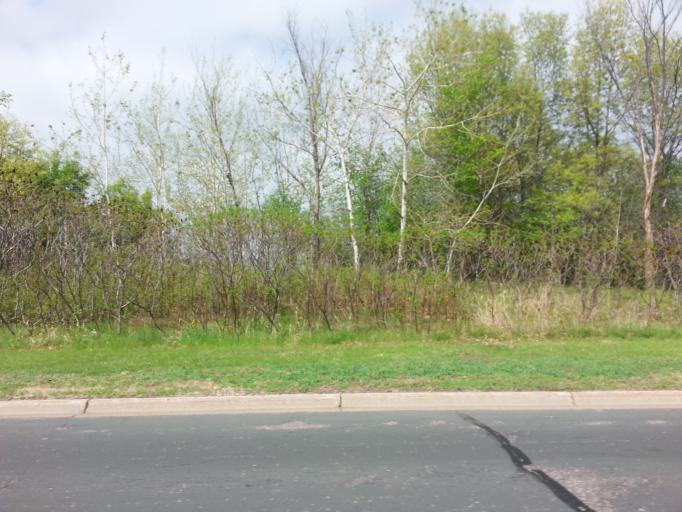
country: US
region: Minnesota
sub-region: Washington County
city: Woodbury
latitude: 44.9299
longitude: -92.9687
